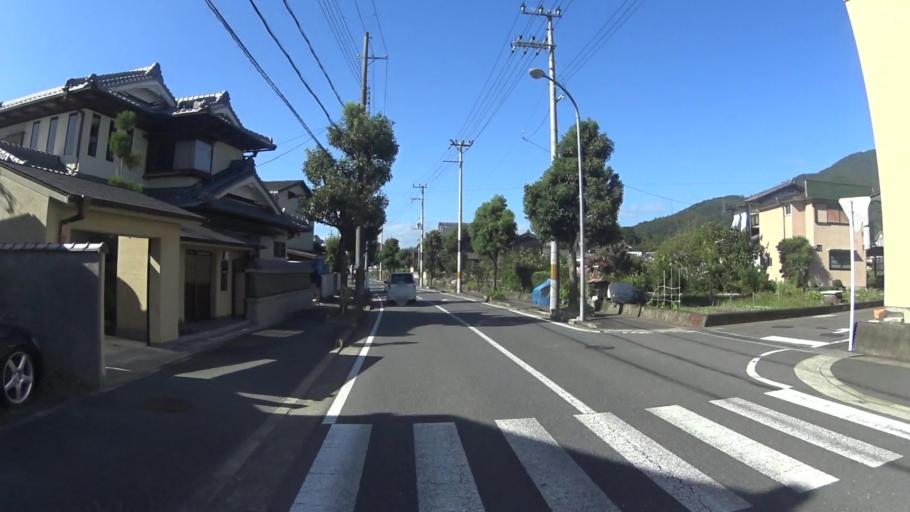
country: JP
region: Kyoto
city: Kameoka
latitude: 35.0257
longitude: 135.5875
